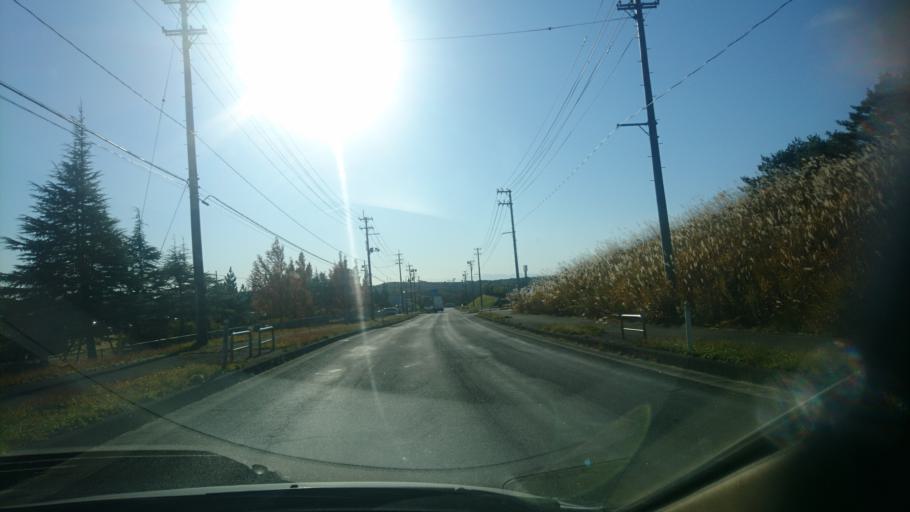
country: JP
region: Miyagi
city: Tomiya
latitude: 38.4566
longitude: 140.9356
